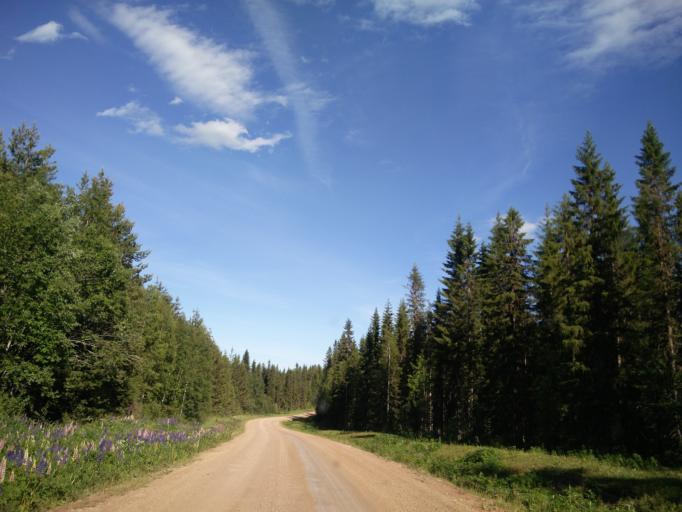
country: SE
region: Gaevleborg
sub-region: Hudiksvalls Kommun
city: Delsbo
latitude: 62.1793
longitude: 16.4879
